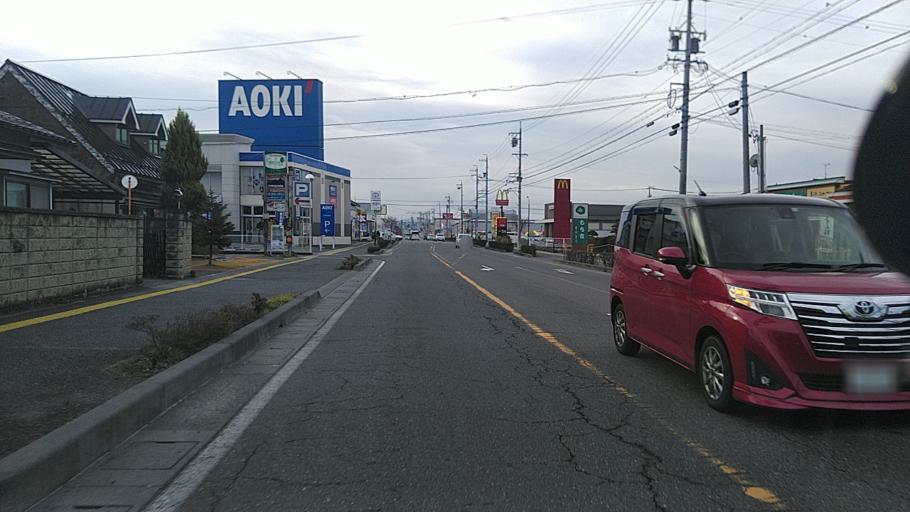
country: JP
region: Nagano
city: Matsumoto
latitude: 36.2217
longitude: 137.9798
